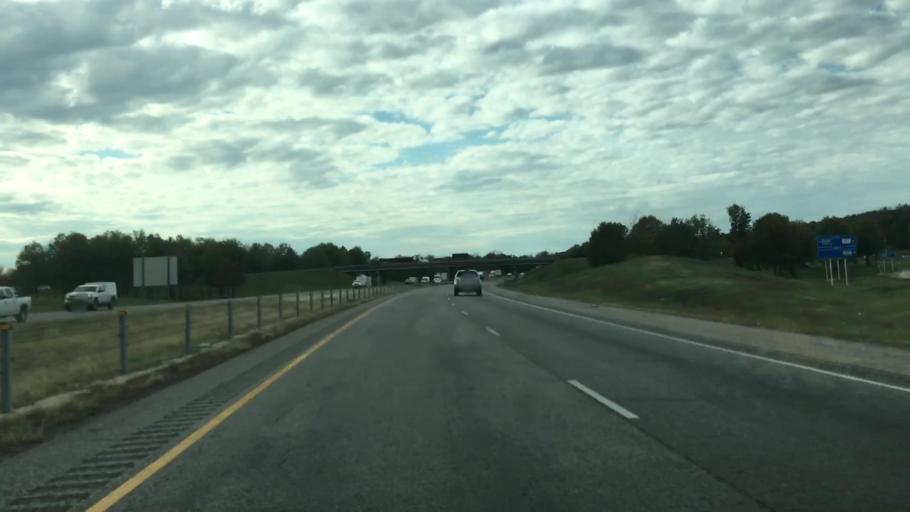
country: US
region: Arkansas
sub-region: Conway County
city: Morrilton
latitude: 35.1746
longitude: -92.7413
